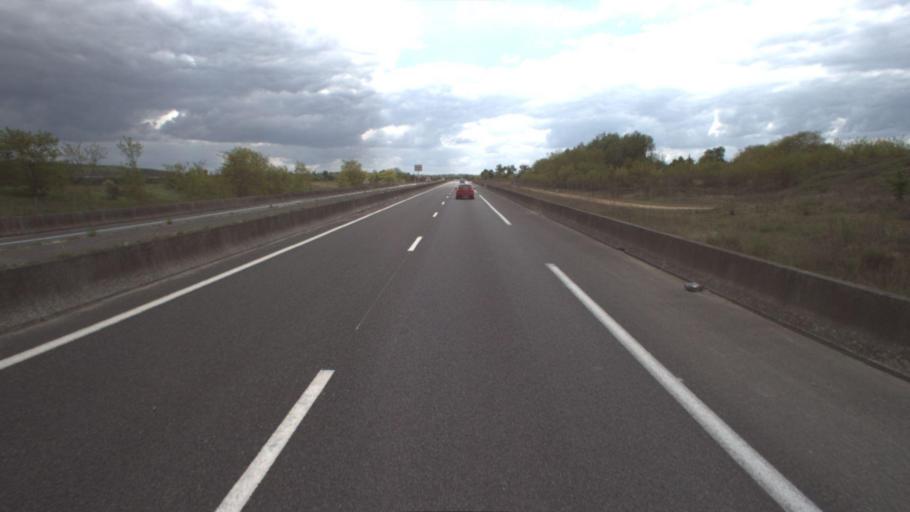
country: FR
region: Ile-de-France
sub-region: Departement de Seine-et-Marne
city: Mareuil-les-Meaux
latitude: 48.9299
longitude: 2.8455
